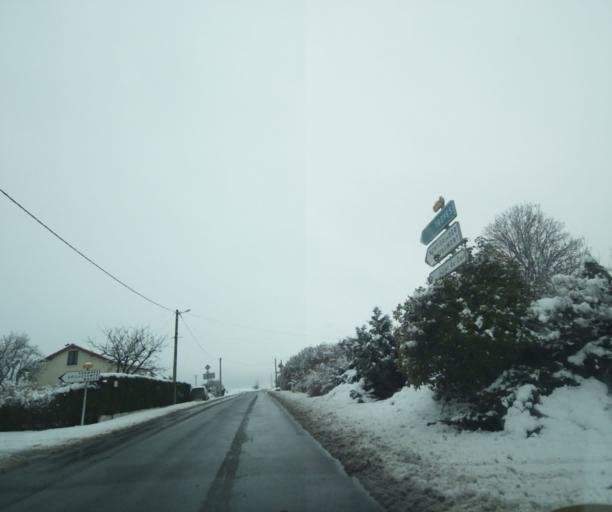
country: FR
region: Champagne-Ardenne
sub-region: Departement de la Haute-Marne
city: Montier-en-Der
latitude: 48.5320
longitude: 4.8164
